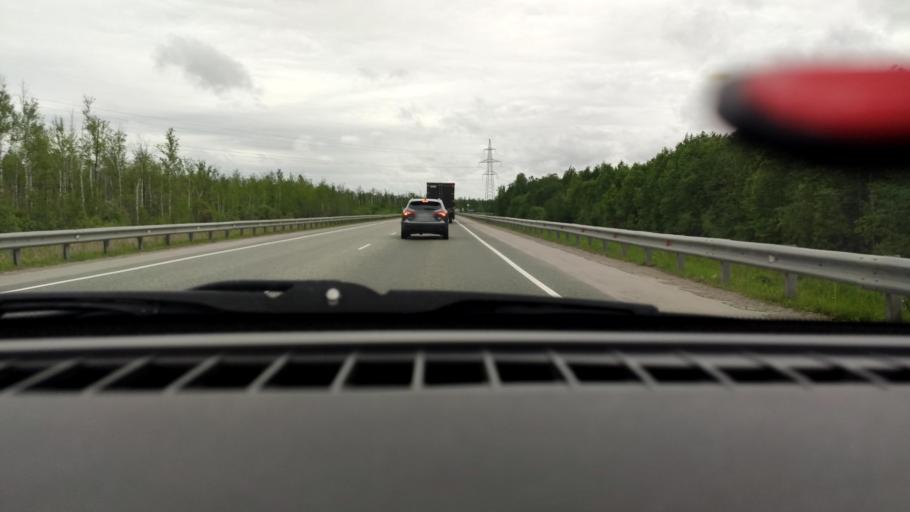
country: RU
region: Perm
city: Krasnokamsk
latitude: 58.1078
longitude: 55.7878
